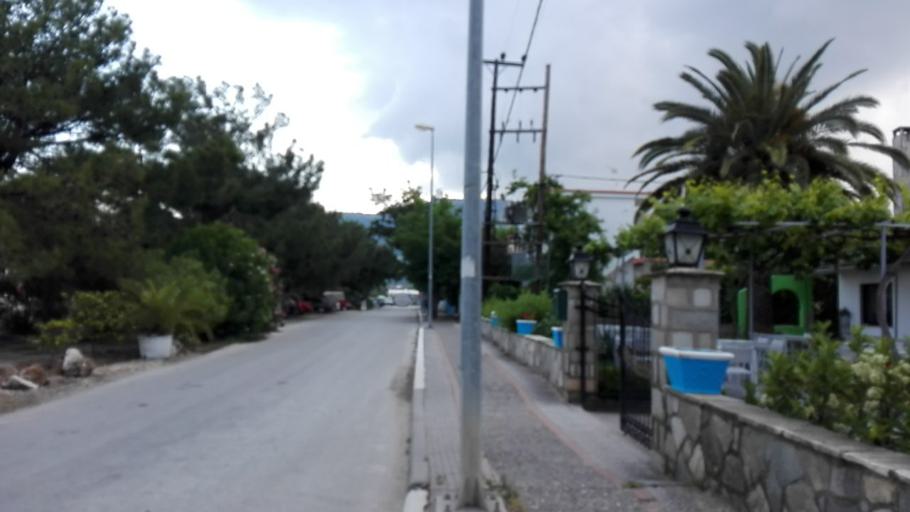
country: GR
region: East Macedonia and Thrace
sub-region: Nomos Kavalas
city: Prinos
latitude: 40.7589
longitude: 24.5744
